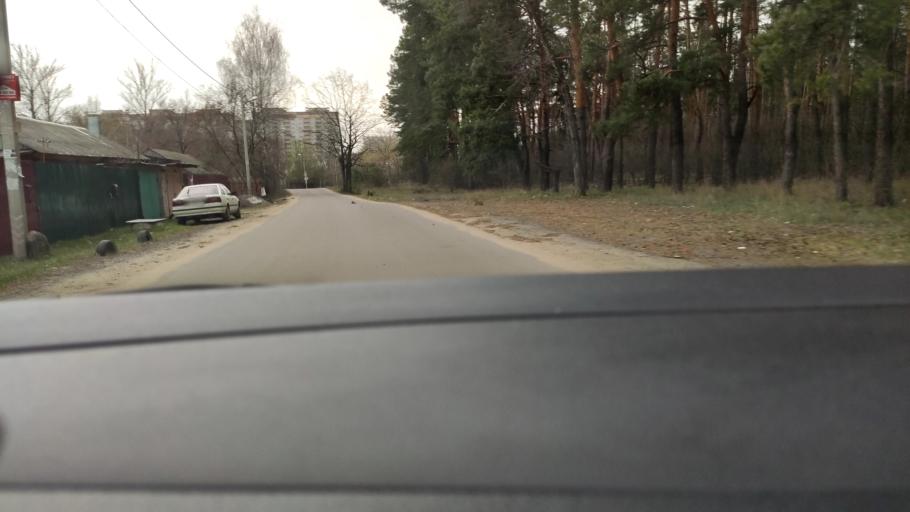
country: RU
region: Voronezj
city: Podgornoye
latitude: 51.7372
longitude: 39.1871
